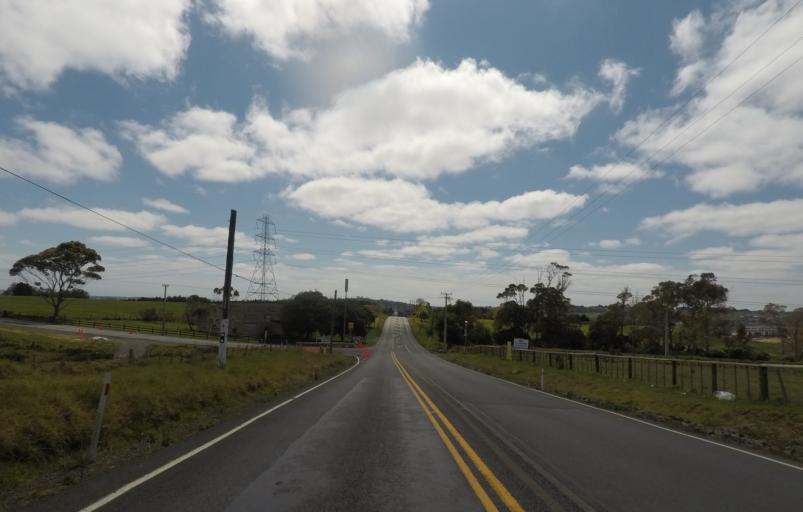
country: NZ
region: Auckland
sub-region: Auckland
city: Manukau City
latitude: -36.9869
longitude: 174.9192
